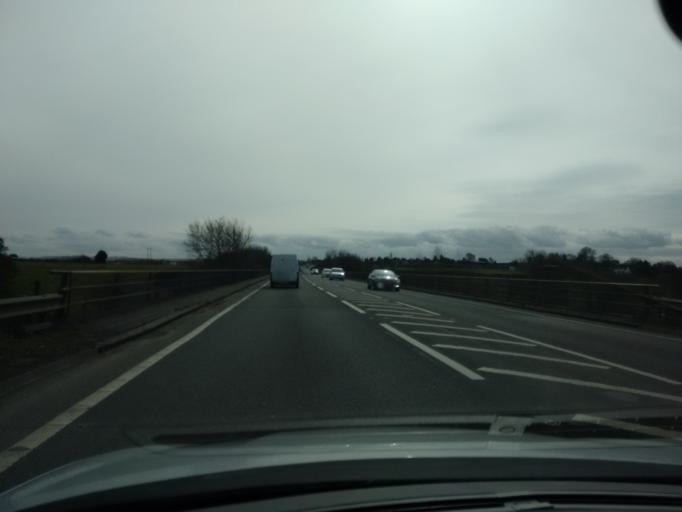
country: GB
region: England
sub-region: Worcestershire
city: Evesham
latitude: 52.1064
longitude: -1.9298
